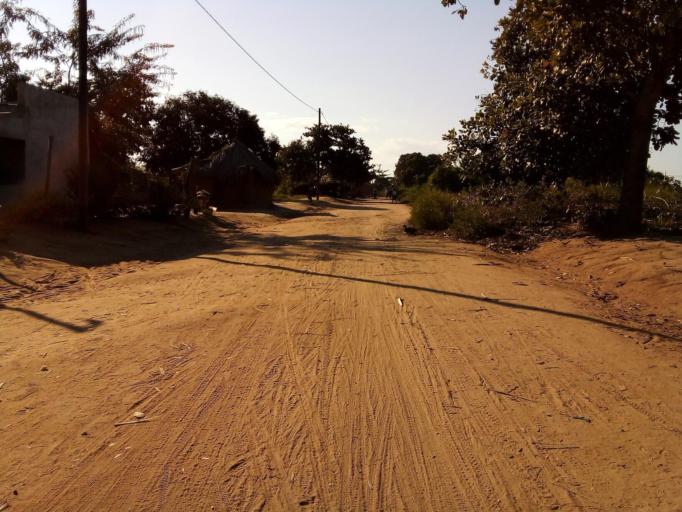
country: MZ
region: Zambezia
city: Quelimane
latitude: -17.5575
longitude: 36.6986
